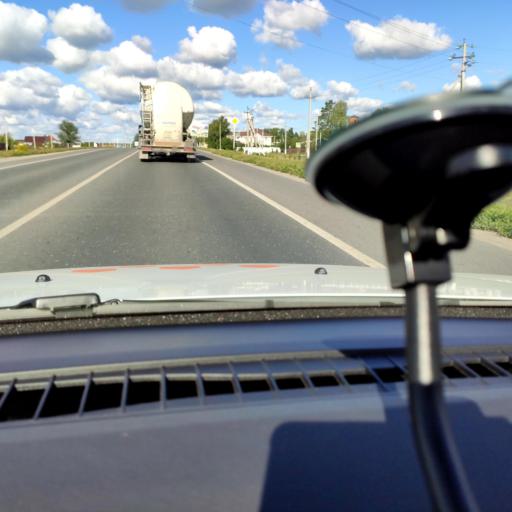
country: RU
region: Samara
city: Kurumoch
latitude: 53.4836
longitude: 50.0364
